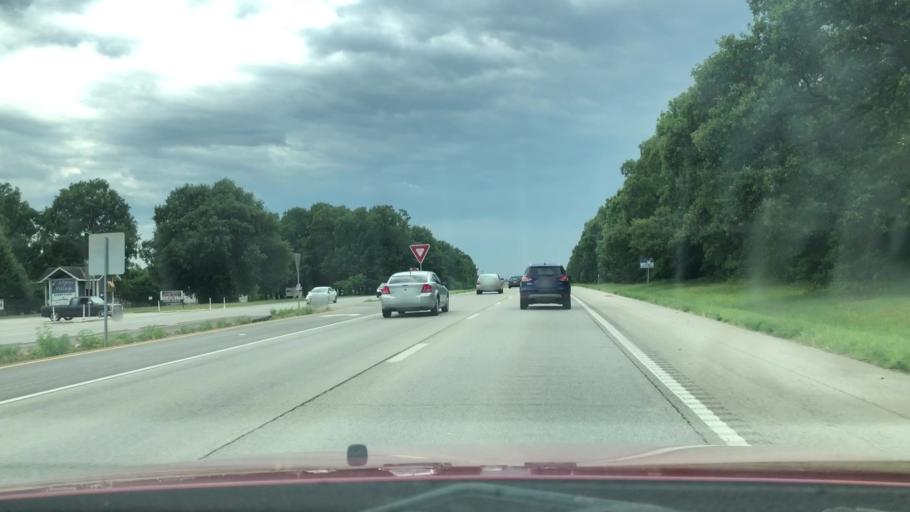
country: US
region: Missouri
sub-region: Greene County
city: Republic
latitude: 37.1392
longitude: -93.4441
